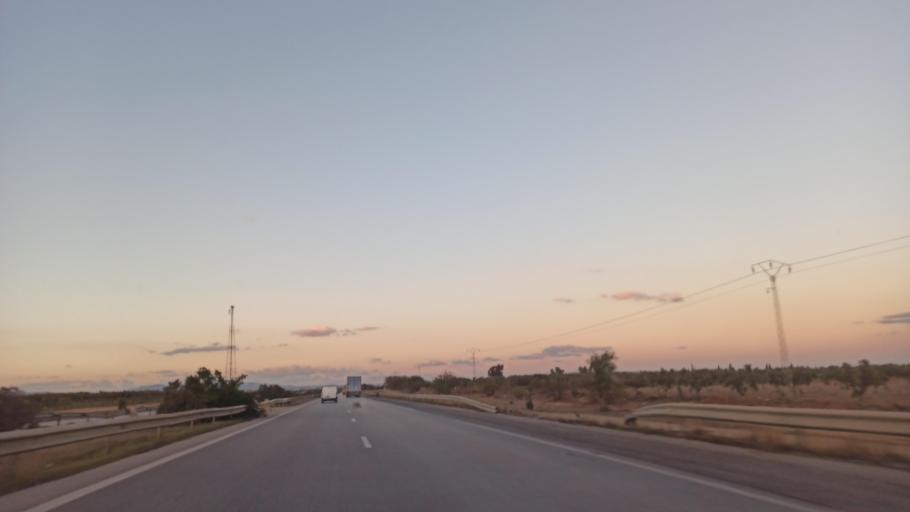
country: TN
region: Nabul
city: Al Hammamat
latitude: 36.2645
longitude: 10.4301
